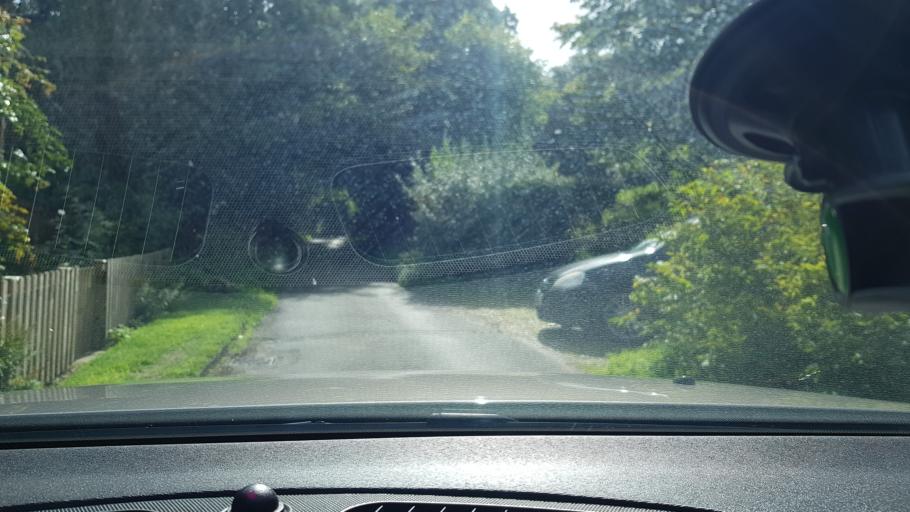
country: GB
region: England
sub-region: Hampshire
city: Highclere
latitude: 51.3388
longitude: -1.3392
